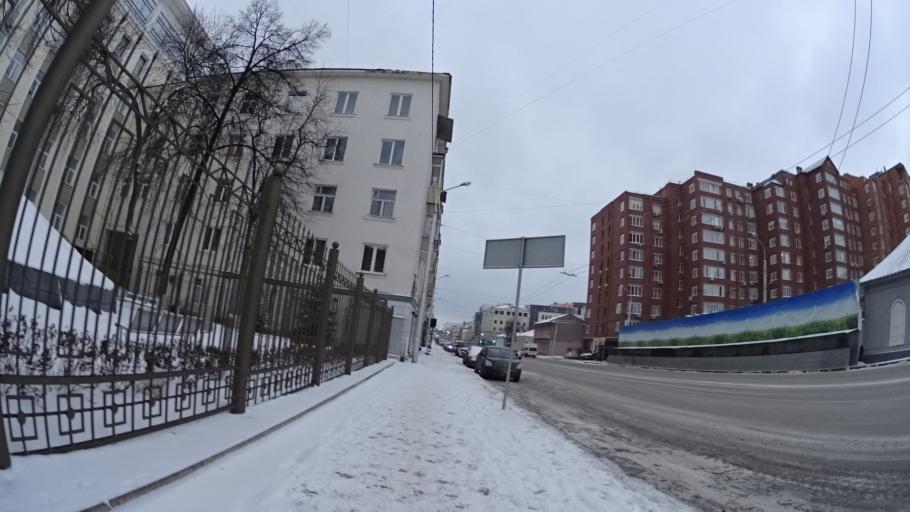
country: RU
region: Bashkortostan
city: Ufa
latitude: 54.7314
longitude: 55.9433
